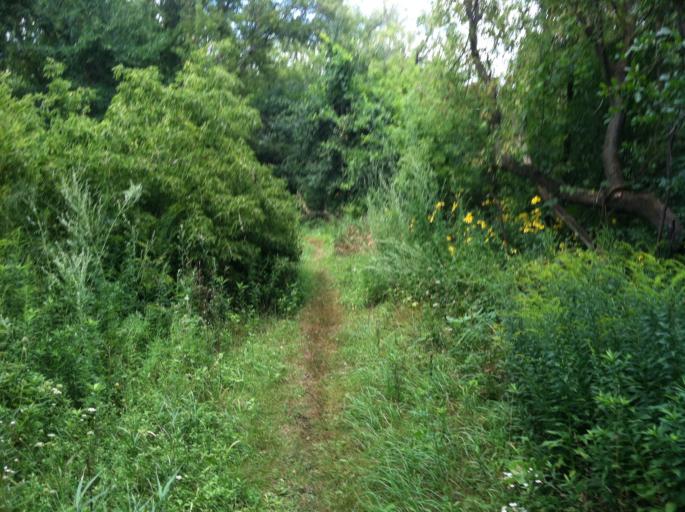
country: US
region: Illinois
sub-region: Cook County
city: Wheeling
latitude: 42.1503
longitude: -87.9105
